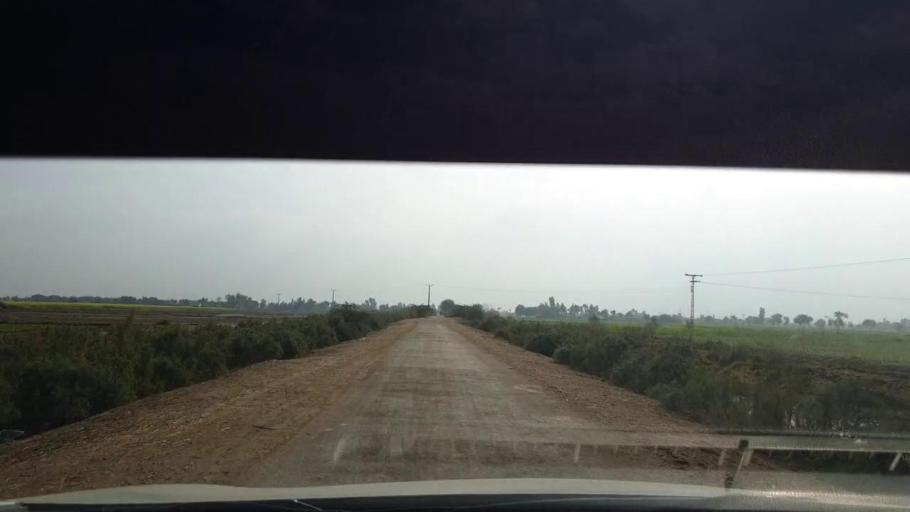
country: PK
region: Sindh
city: Berani
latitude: 25.7638
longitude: 68.8765
